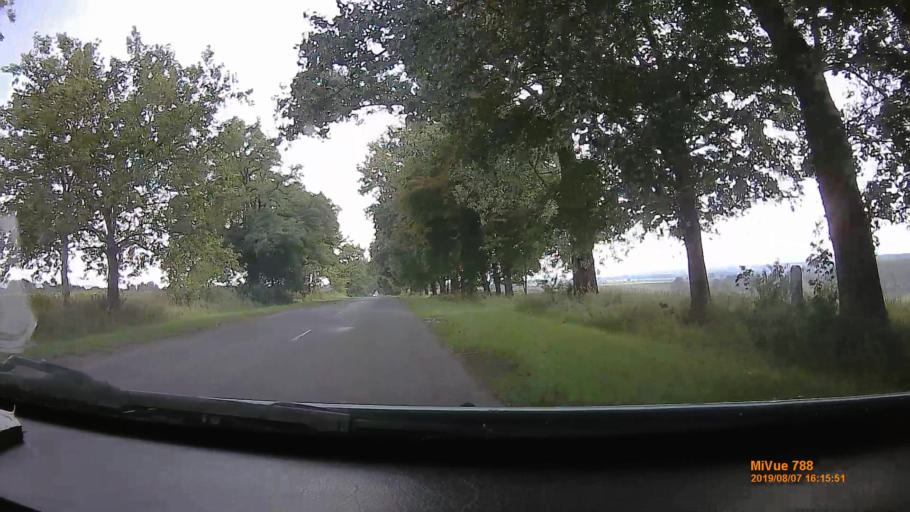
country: HU
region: Borsod-Abauj-Zemplen
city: Gonc
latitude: 48.4666
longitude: 21.2529
